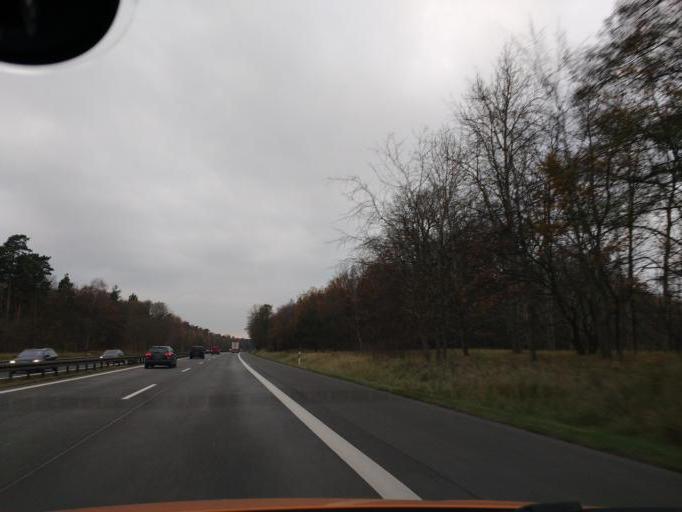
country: DE
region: Brandenburg
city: Fehrbellin
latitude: 52.7574
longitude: 12.8417
